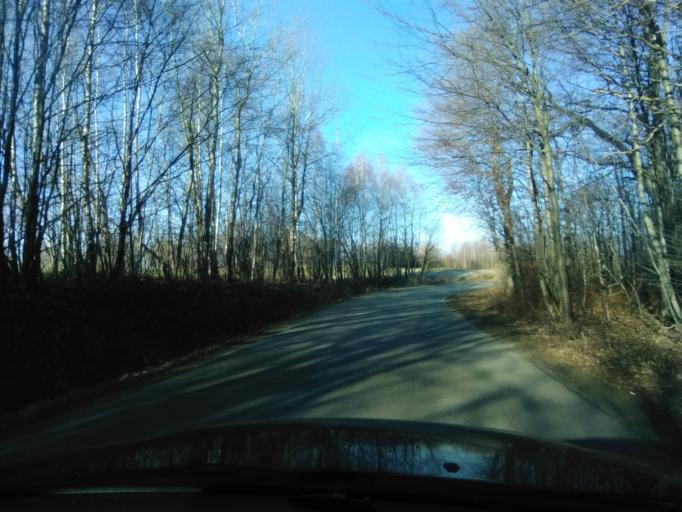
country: PL
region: Subcarpathian Voivodeship
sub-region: Powiat krosnienski
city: Rymanow
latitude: 49.5938
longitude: 21.8932
